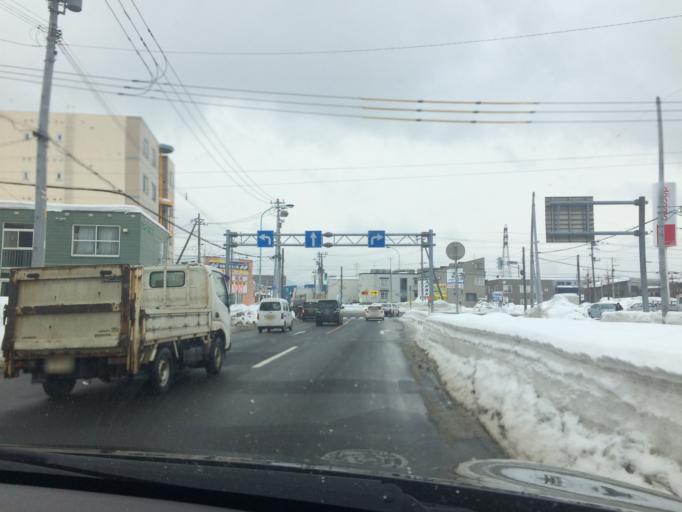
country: JP
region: Hokkaido
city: Sapporo
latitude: 43.0560
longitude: 141.4268
